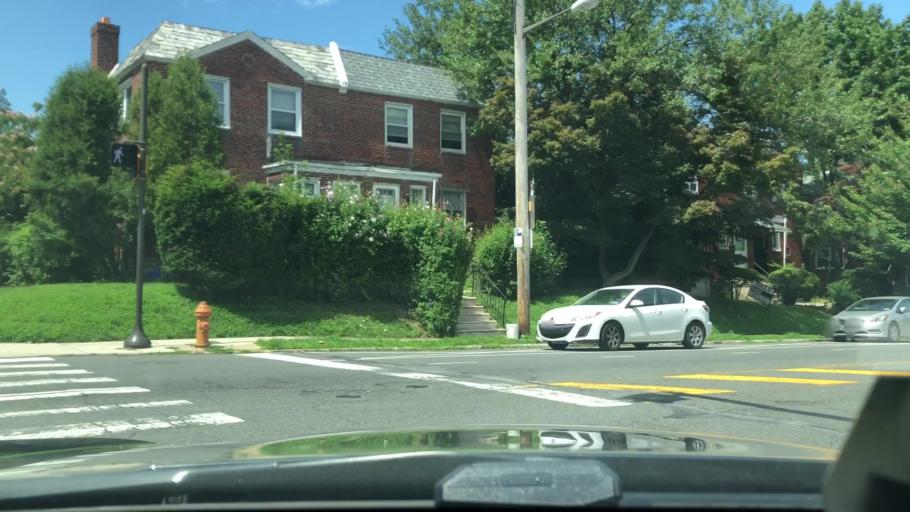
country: US
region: Pennsylvania
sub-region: Montgomery County
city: Wyndmoor
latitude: 40.0625
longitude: -75.1706
